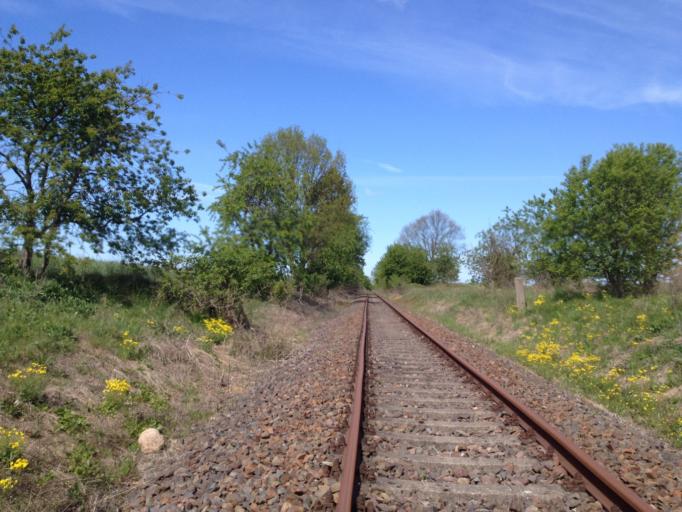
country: DE
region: Brandenburg
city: Templin
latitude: 53.1146
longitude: 13.4618
